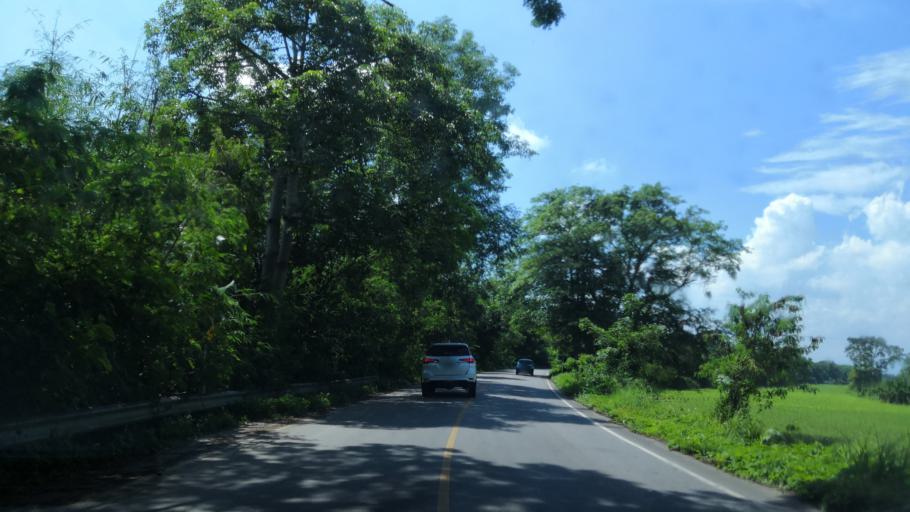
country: TH
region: Chiang Rai
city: Wiang Chai
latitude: 19.9460
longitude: 99.9311
